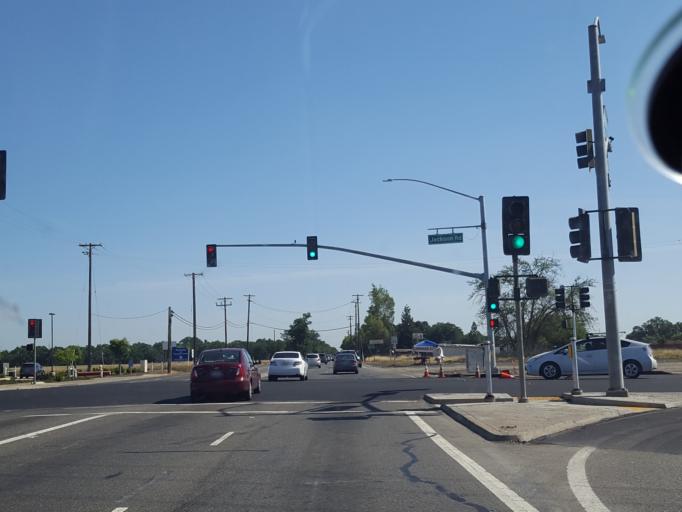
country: US
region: California
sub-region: Sacramento County
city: Rosemont
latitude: 38.5294
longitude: -121.3351
